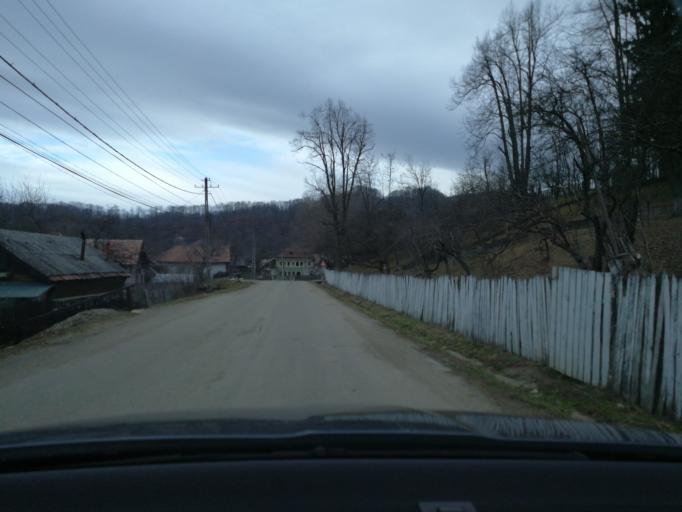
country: RO
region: Dambovita
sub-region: Comuna Bezdead
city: Bezdead
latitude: 45.1672
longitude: 25.5411
